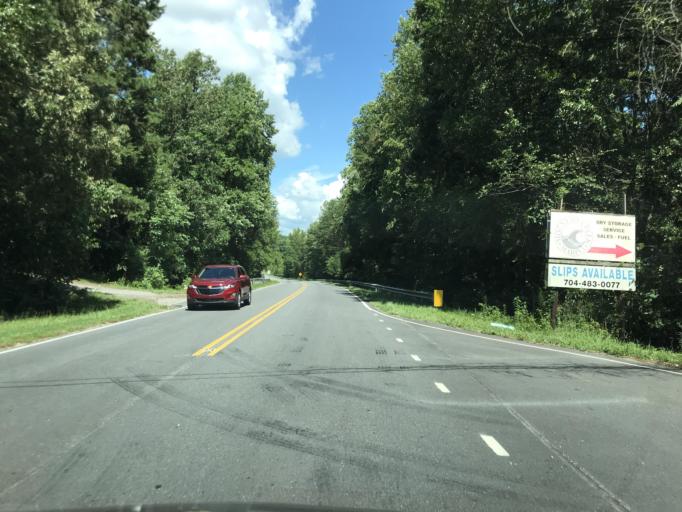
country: US
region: North Carolina
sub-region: Catawba County
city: Lake Norman of Catawba
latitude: 35.5757
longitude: -81.0063
